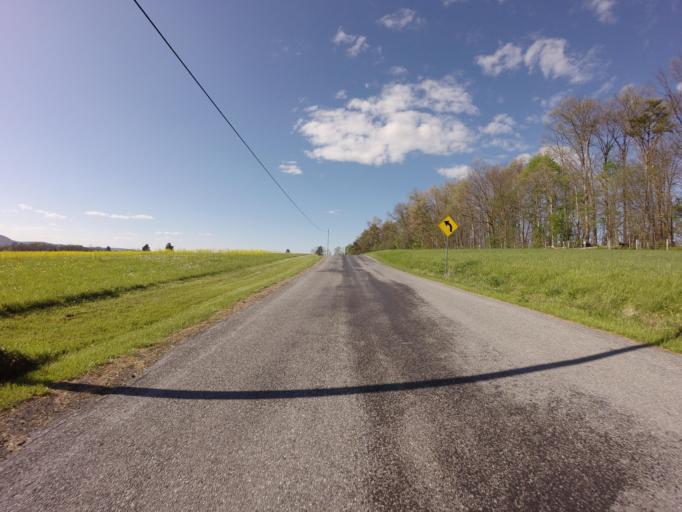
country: US
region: Maryland
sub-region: Frederick County
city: Emmitsburg
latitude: 39.6586
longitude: -77.2824
